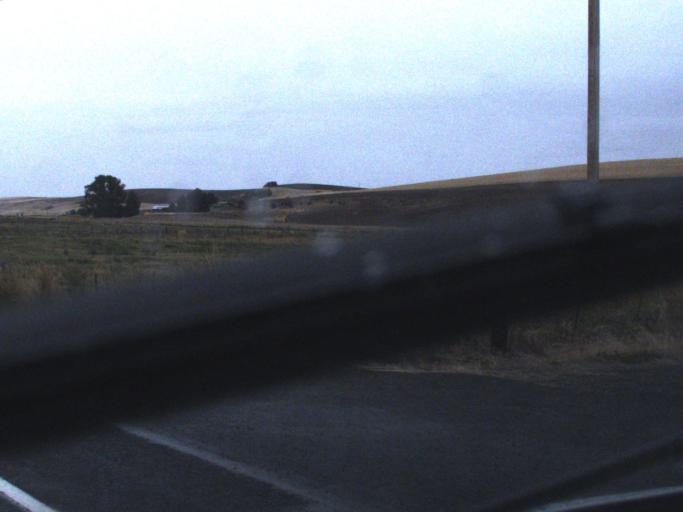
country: US
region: Washington
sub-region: Whitman County
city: Colfax
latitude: 46.8042
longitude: -117.5662
